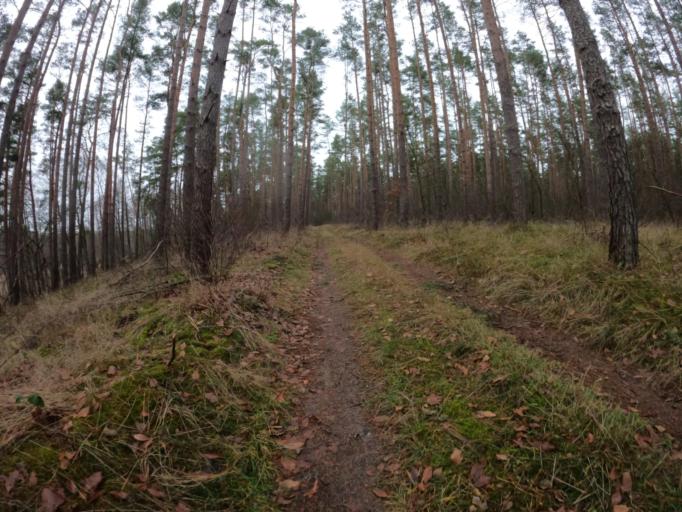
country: PL
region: West Pomeranian Voivodeship
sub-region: Powiat mysliborski
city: Debno
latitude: 52.7285
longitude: 14.7536
